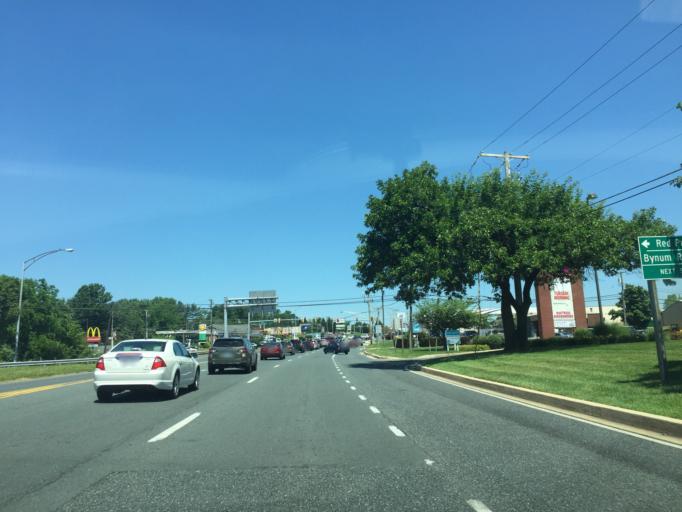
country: US
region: Maryland
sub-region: Harford County
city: Bel Air North
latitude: 39.5570
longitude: -76.3693
